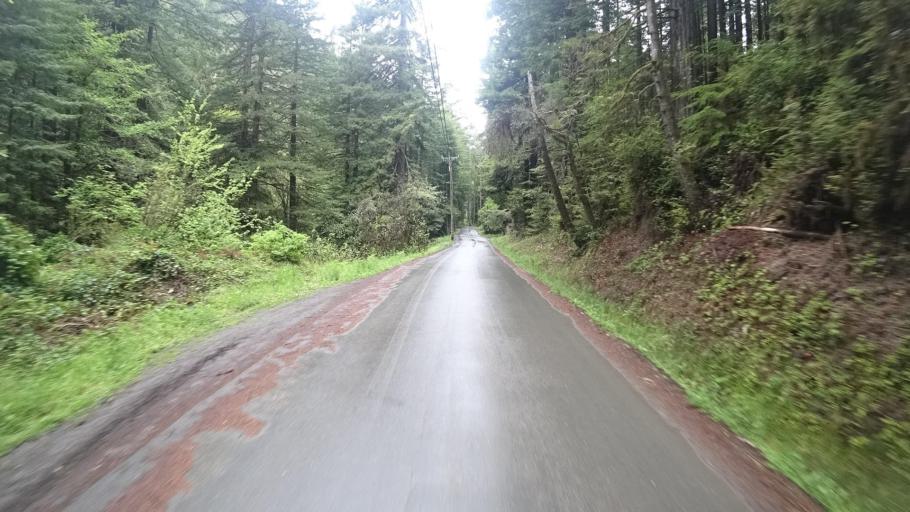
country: US
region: California
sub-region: Humboldt County
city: Bayside
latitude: 40.8119
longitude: -124.0243
